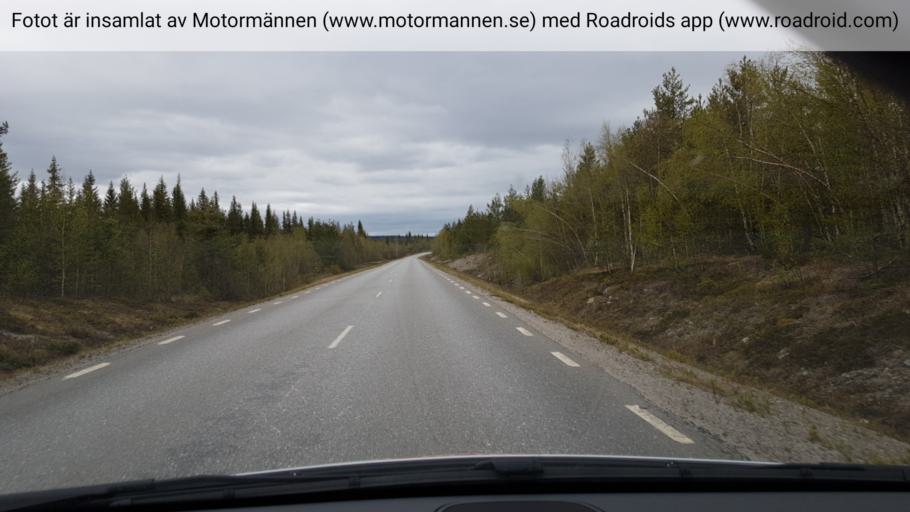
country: SE
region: Vaesterbotten
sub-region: Sorsele Kommun
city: Sorsele
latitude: 65.5129
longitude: 17.3089
